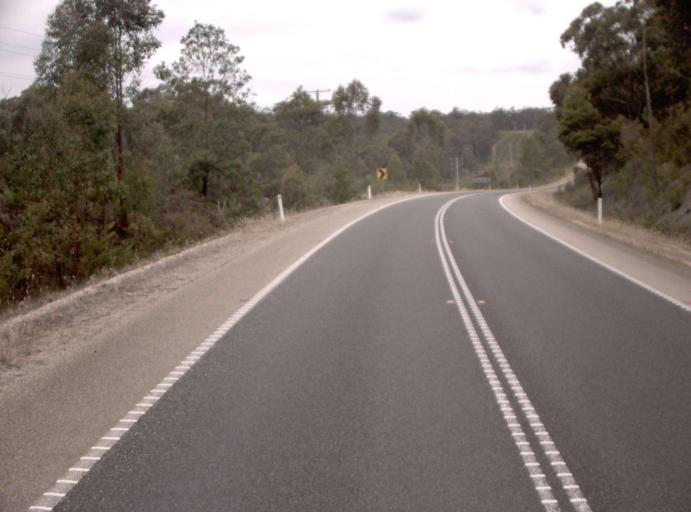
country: AU
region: Victoria
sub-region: East Gippsland
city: Lakes Entrance
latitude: -37.6897
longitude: 148.0312
